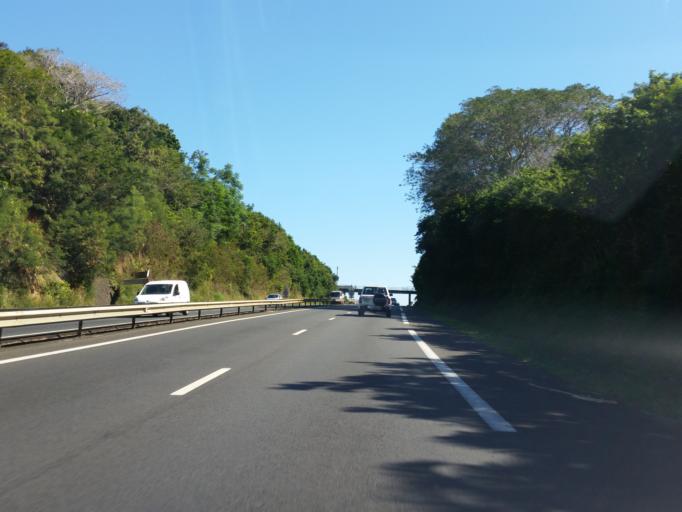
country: RE
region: Reunion
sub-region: Reunion
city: Sainte-Marie
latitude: -20.8979
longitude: 55.5728
